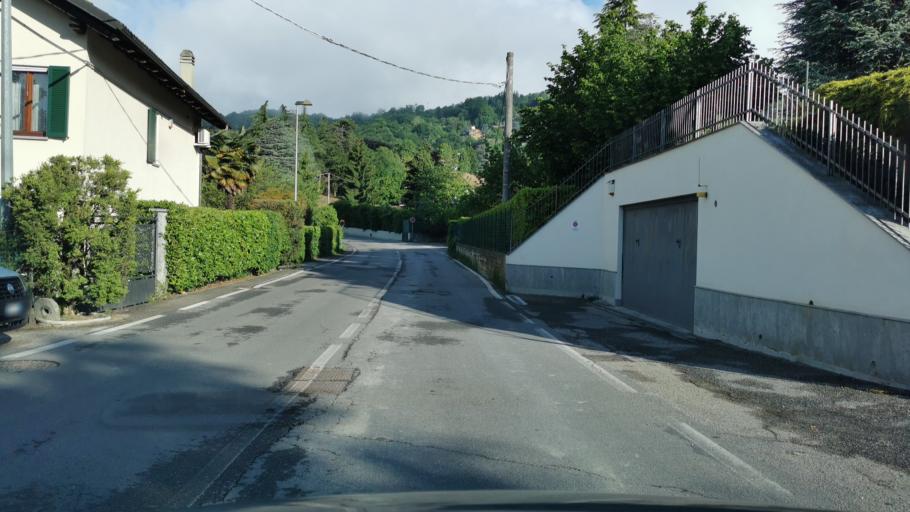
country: IT
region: Piedmont
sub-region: Provincia di Torino
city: Pino Torinese
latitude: 45.0346
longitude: 7.7728
